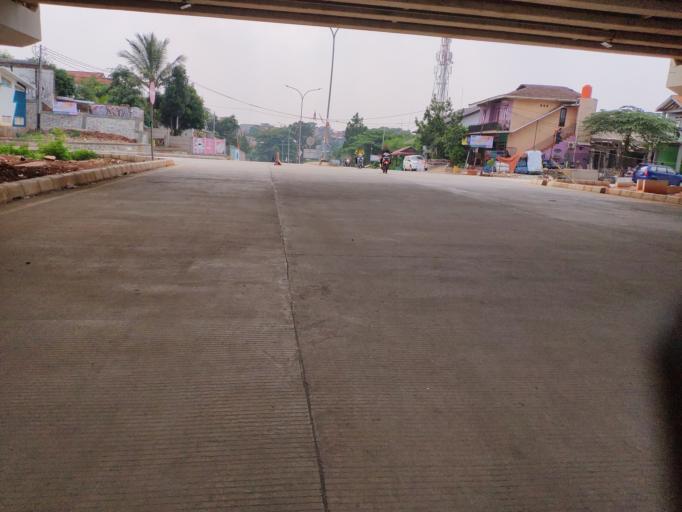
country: ID
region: West Java
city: Pamulang
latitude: -6.3245
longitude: 106.8024
